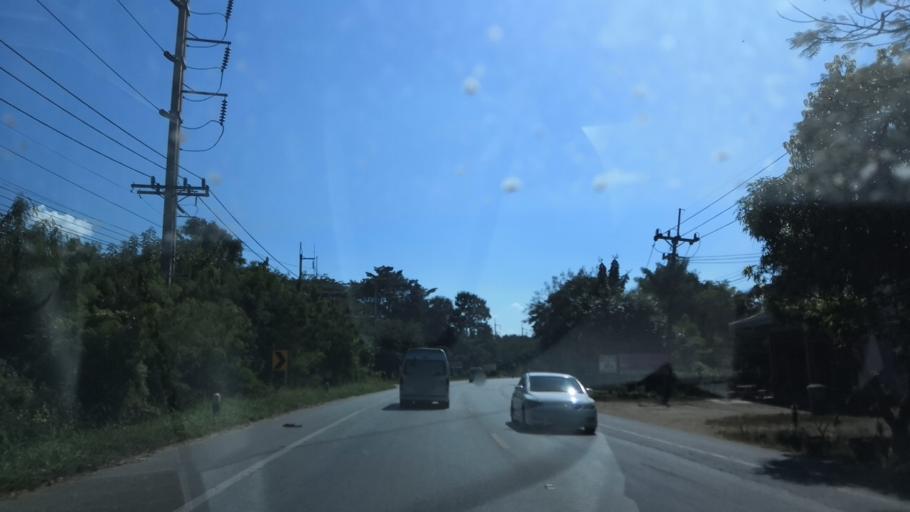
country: TH
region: Chiang Rai
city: Mae Suai
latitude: 19.5615
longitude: 99.4940
